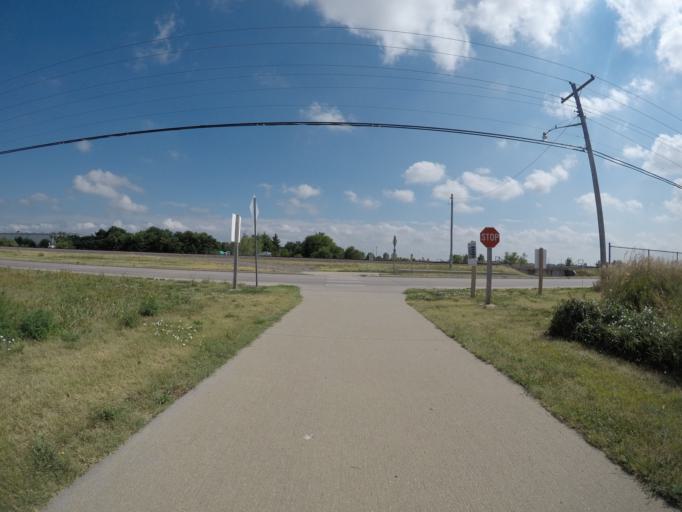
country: US
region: Nebraska
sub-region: Buffalo County
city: Kearney
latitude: 40.6934
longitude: -99.1043
